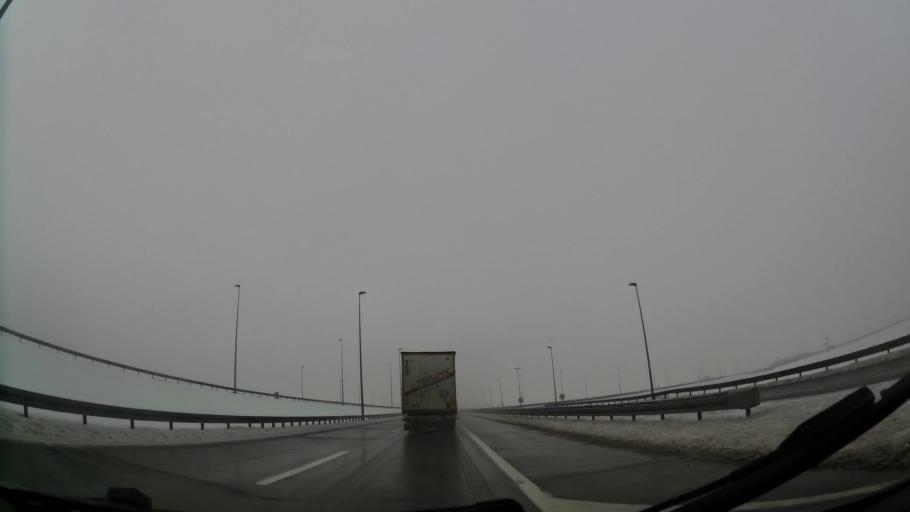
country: RS
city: Dobanovci
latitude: 44.8326
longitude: 20.2512
